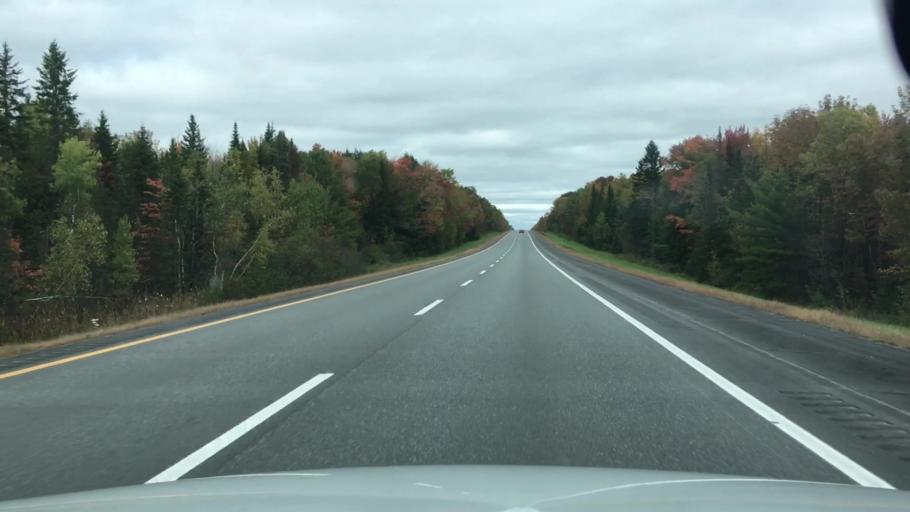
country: US
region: Maine
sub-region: Waldo County
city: Burnham
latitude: 44.7219
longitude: -69.4414
